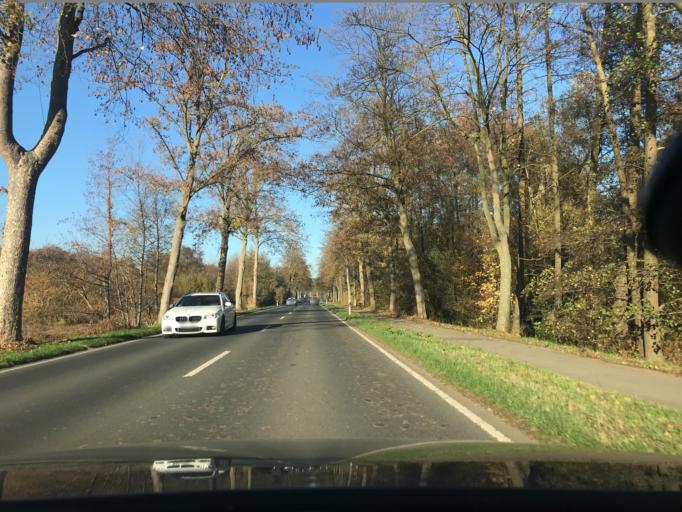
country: DE
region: North Rhine-Westphalia
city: Kempen
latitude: 51.4145
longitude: 6.4181
